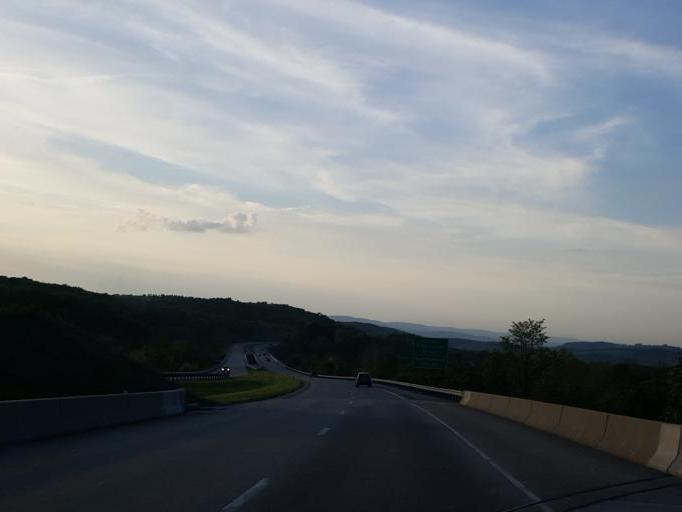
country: US
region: Pennsylvania
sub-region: Blair County
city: Roaring Spring
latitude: 40.3381
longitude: -78.4295
